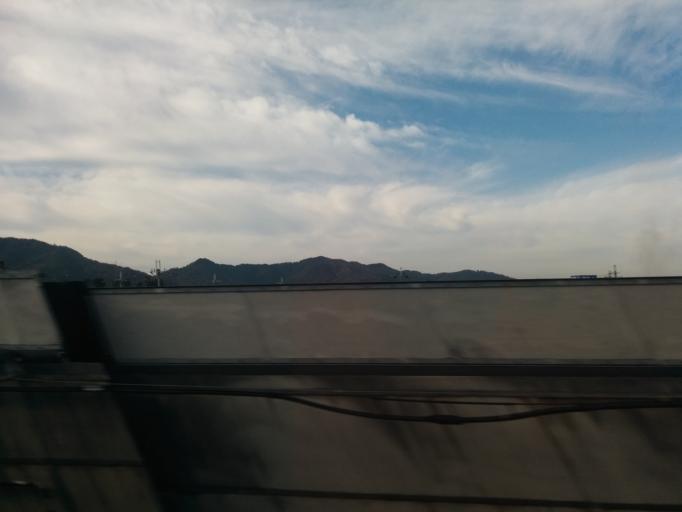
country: JP
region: Shiga Prefecture
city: Youkaichi
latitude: 35.1457
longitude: 136.1874
